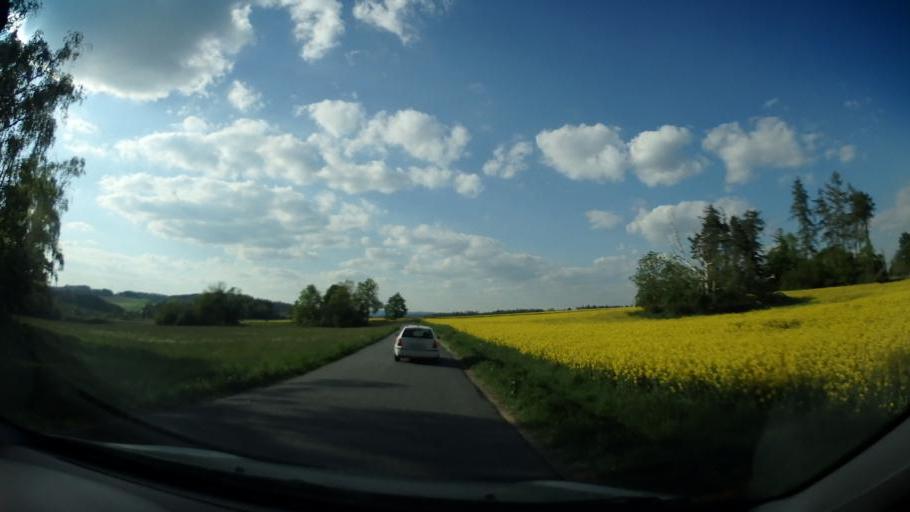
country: CZ
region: Vysocina
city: Budisov
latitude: 49.3120
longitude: 15.9737
